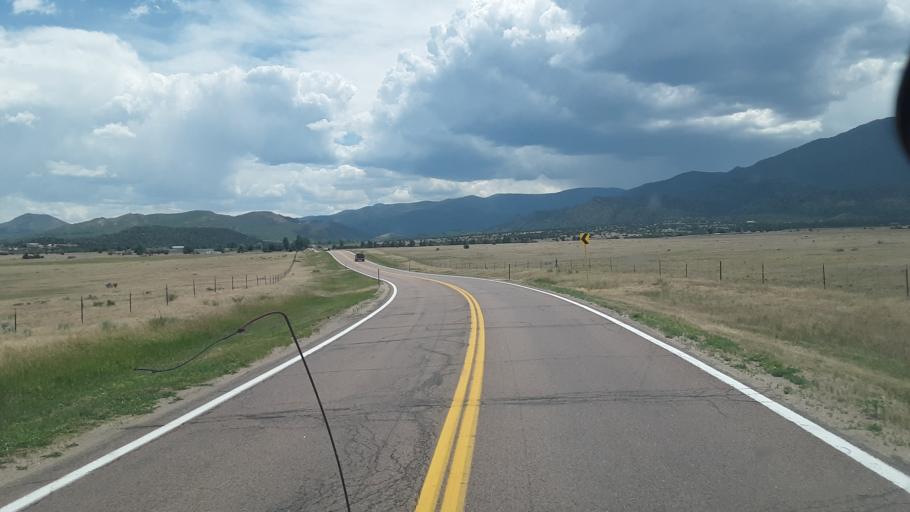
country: US
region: Colorado
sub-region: Fremont County
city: Florence
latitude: 38.2562
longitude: -105.0901
